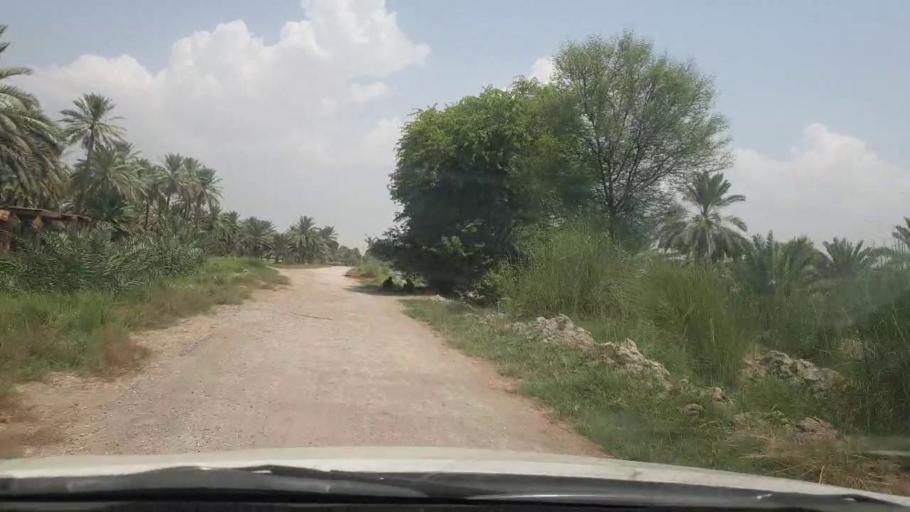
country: PK
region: Sindh
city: Khairpur
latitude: 27.5487
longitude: 68.8451
